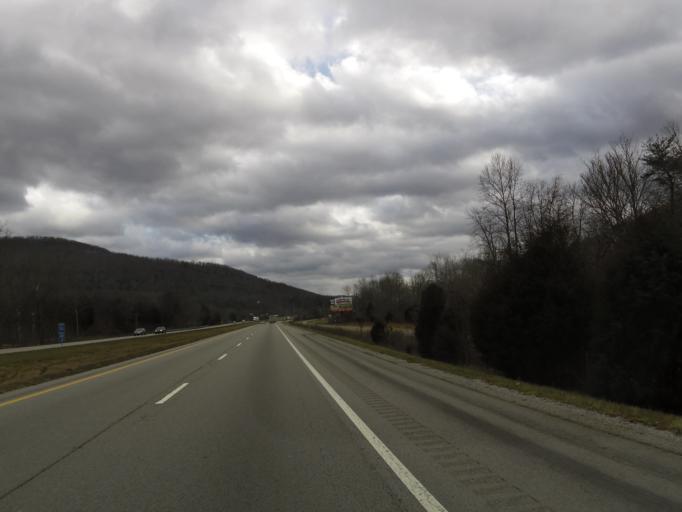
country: US
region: Tennessee
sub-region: Marion County
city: Monteagle
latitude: 35.1521
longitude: -85.7817
